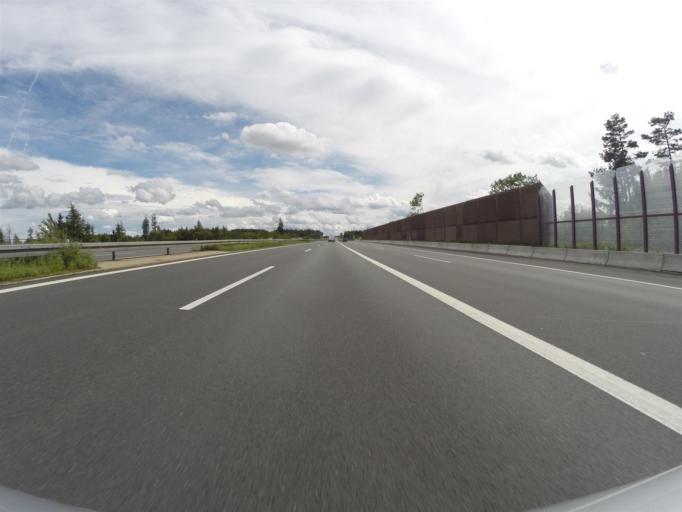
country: DE
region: Bavaria
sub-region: Upper Franconia
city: Leupoldsgrun
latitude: 50.3162
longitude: 11.7985
